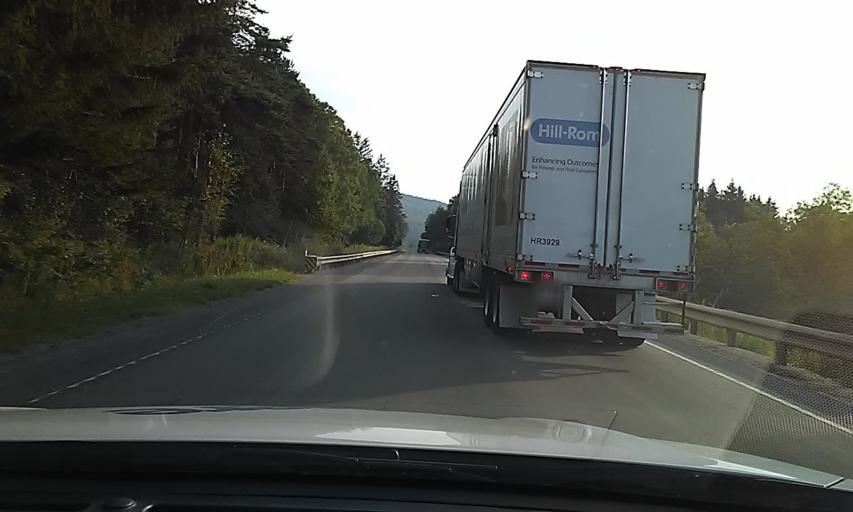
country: US
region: Pennsylvania
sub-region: McKean County
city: Smethport
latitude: 41.7146
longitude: -78.5610
